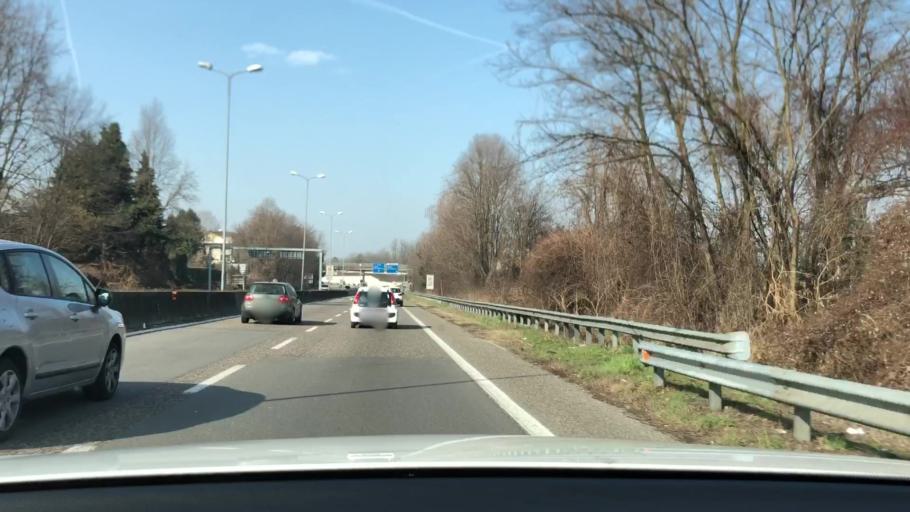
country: IT
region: Lombardy
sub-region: Provincia di Monza e Brianza
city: Barlassina
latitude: 45.6615
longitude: 9.1315
